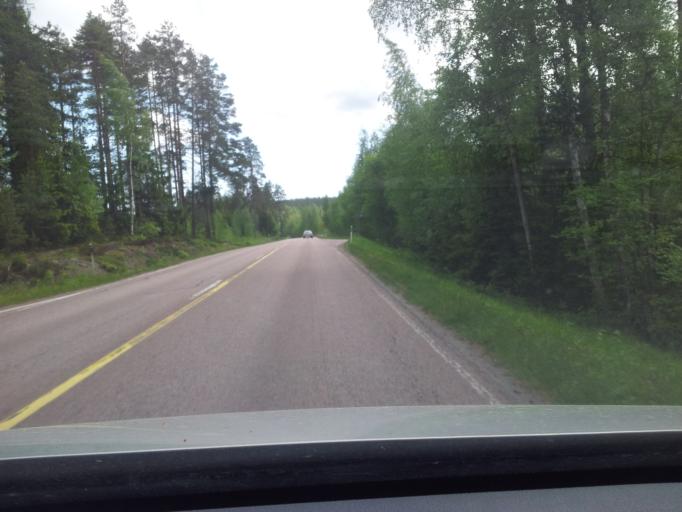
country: FI
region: South Karelia
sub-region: Lappeenranta
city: Luumaeki
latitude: 60.9537
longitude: 27.5784
